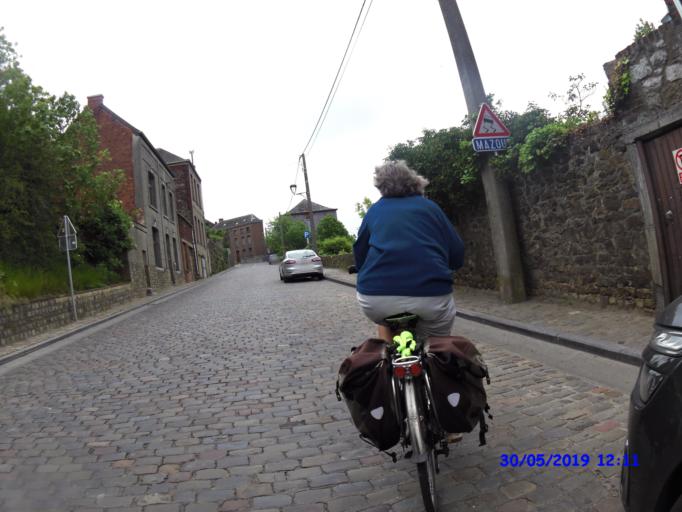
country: BE
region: Wallonia
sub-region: Province du Hainaut
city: Thuin
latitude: 50.3399
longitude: 4.2837
